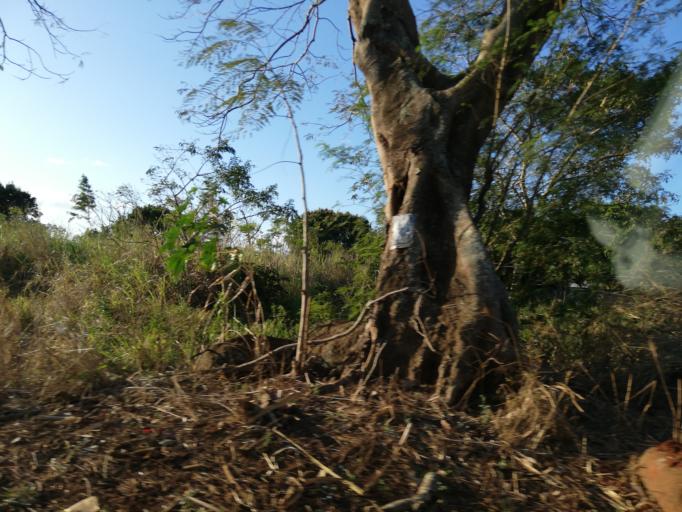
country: MU
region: Pamplemousses
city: Morcellemont Saint Andre
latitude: -20.0794
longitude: 57.5373
